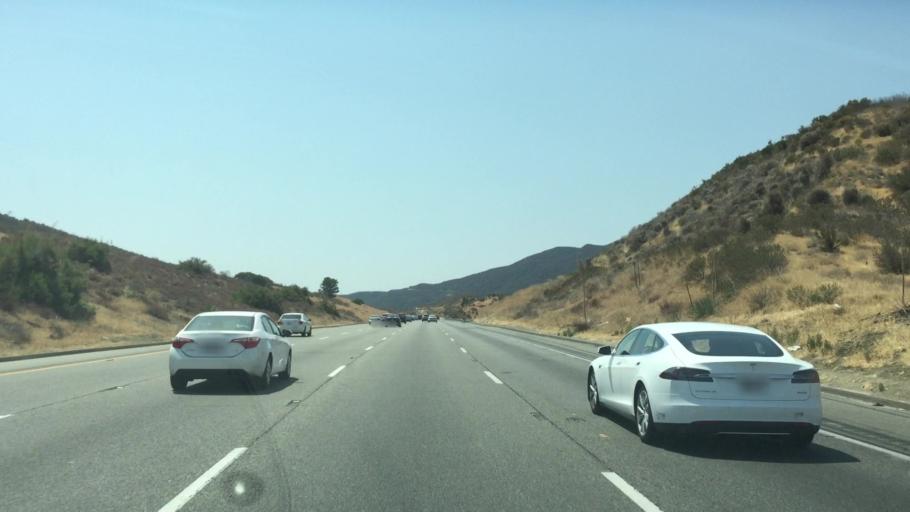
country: US
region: California
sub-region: Los Angeles County
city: Castaic
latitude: 34.6104
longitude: -118.7129
